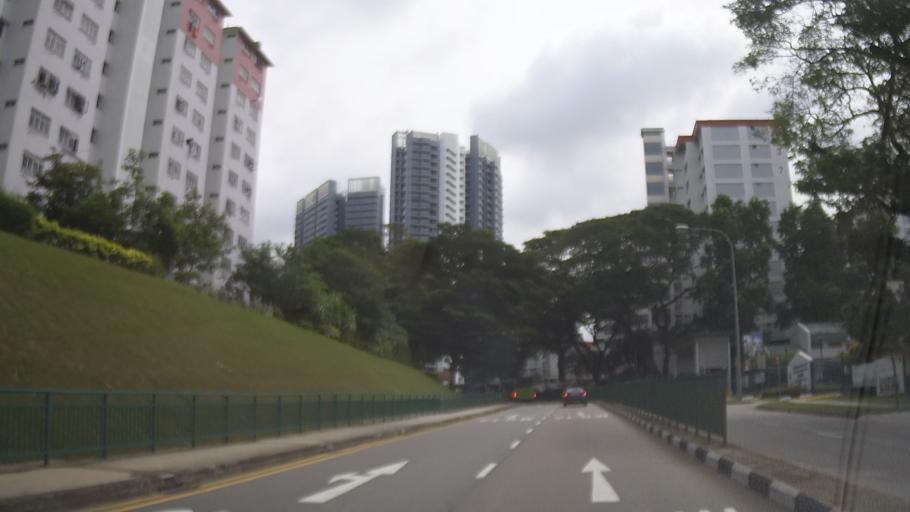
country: MY
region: Johor
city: Johor Bahru
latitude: 1.4387
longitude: 103.7755
